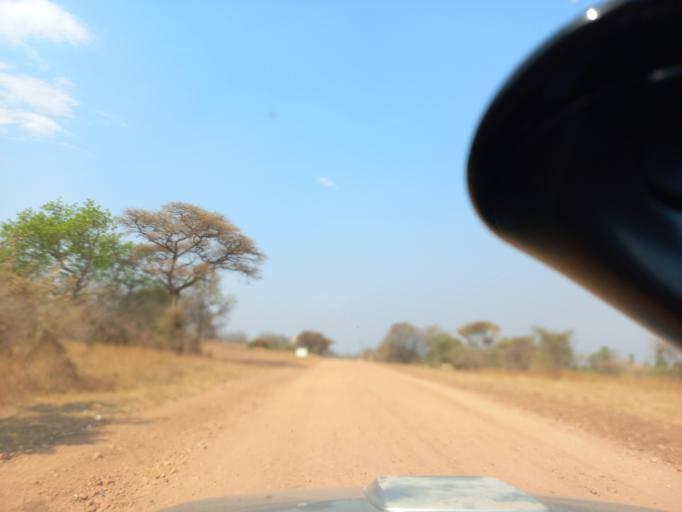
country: ZW
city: Chirundu
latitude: -15.9300
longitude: 28.9648
